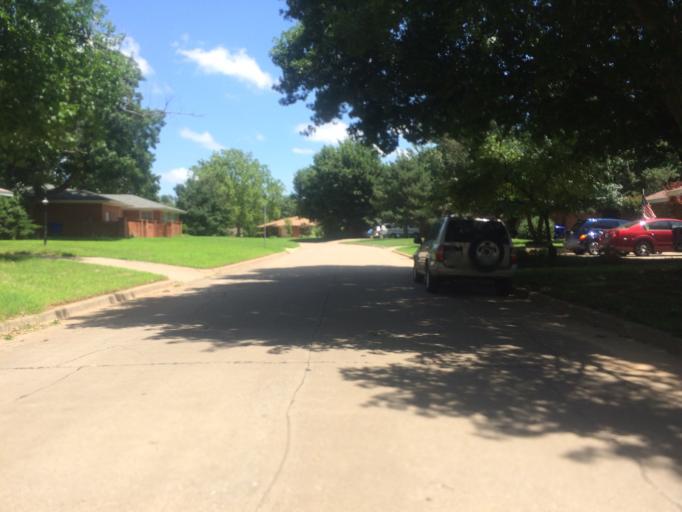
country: US
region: Oklahoma
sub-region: Cleveland County
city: Norman
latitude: 35.2097
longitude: -97.4649
